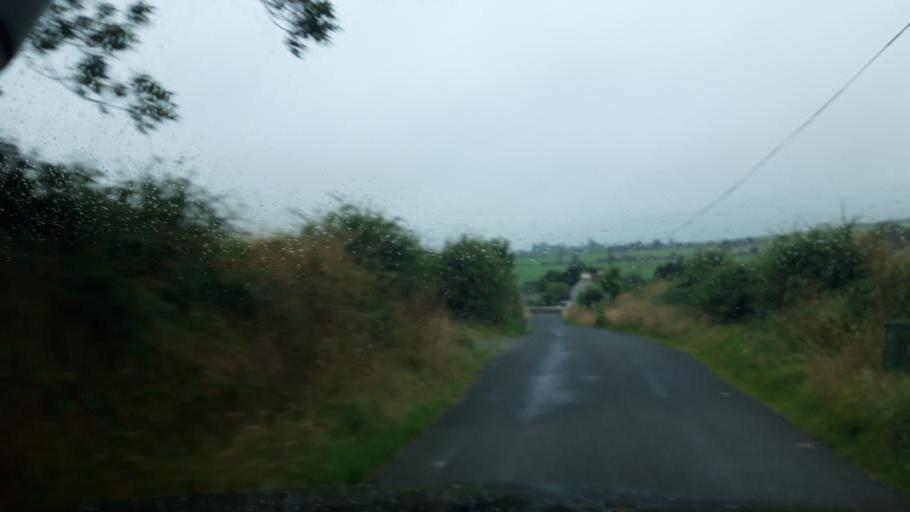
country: IE
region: Leinster
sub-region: Kilkenny
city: Callan
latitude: 52.6304
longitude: -7.5478
